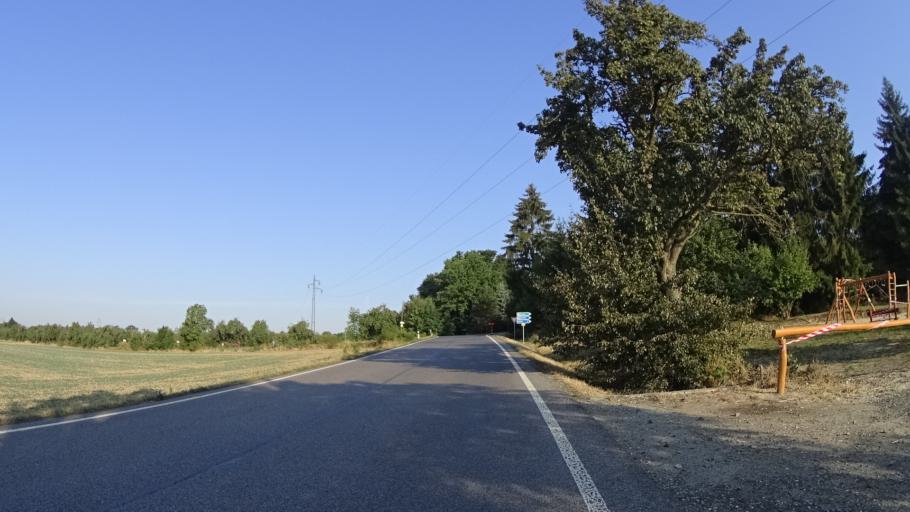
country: CZ
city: Ohrazenice
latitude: 50.5918
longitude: 15.1123
